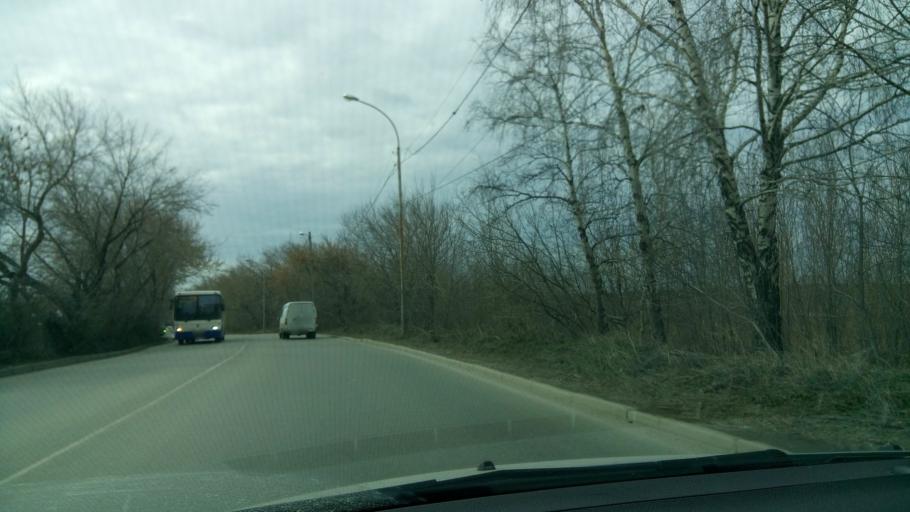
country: RU
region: Sverdlovsk
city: Beryozovsky
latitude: 56.8840
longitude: 60.7072
